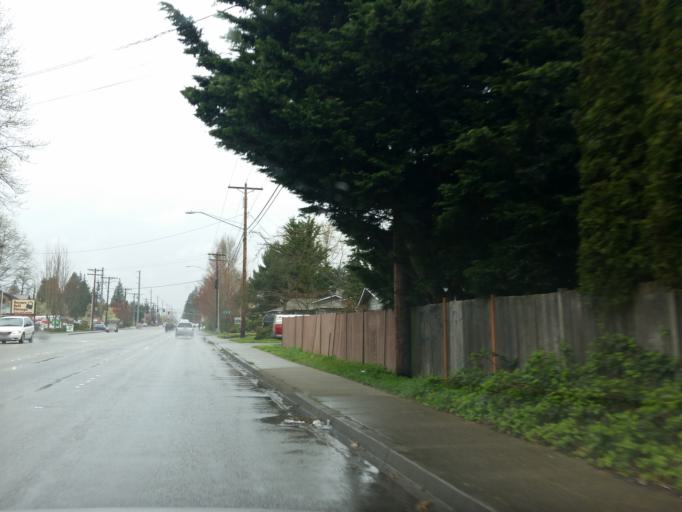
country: US
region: Washington
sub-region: Snohomish County
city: Martha Lake
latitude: 47.8937
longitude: -122.2388
